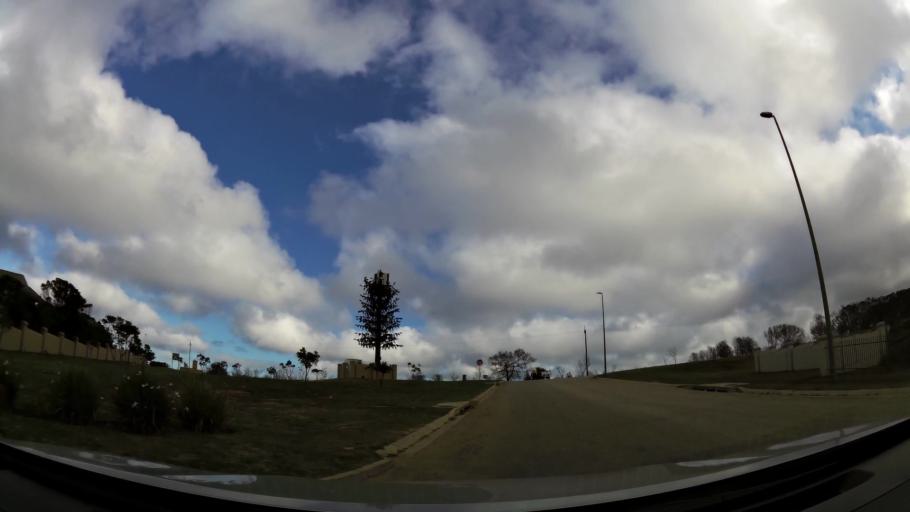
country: ZA
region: Western Cape
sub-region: Eden District Municipality
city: Plettenberg Bay
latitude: -34.0895
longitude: 23.3558
